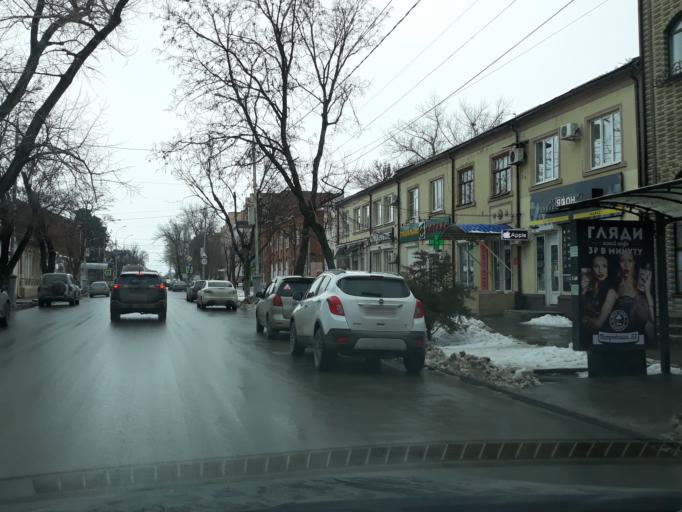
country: RU
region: Rostov
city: Taganrog
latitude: 47.2091
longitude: 38.9389
